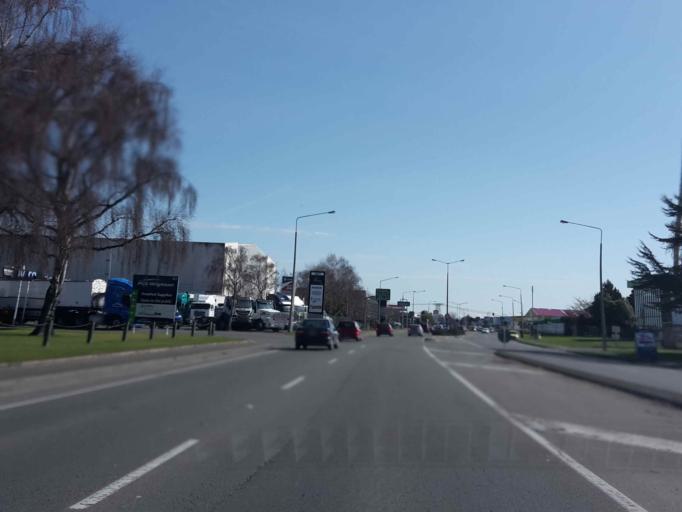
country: NZ
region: Canterbury
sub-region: Christchurch City
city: Christchurch
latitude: -43.5394
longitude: 172.5720
